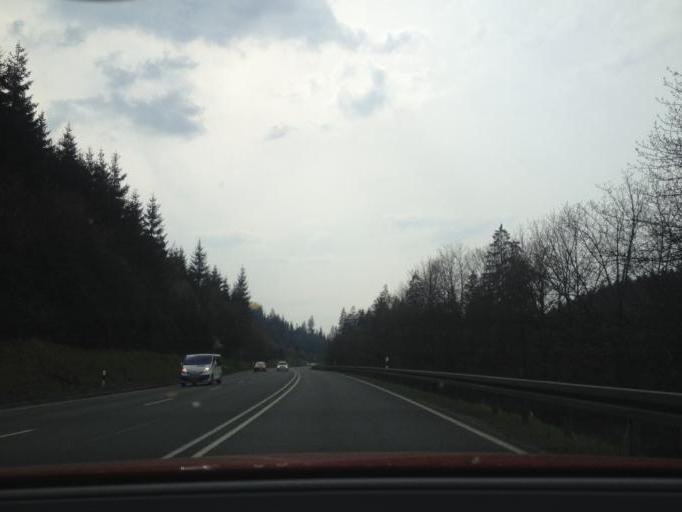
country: DE
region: Bavaria
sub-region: Upper Franconia
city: Bischofsgrun
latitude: 50.0514
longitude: 11.7681
